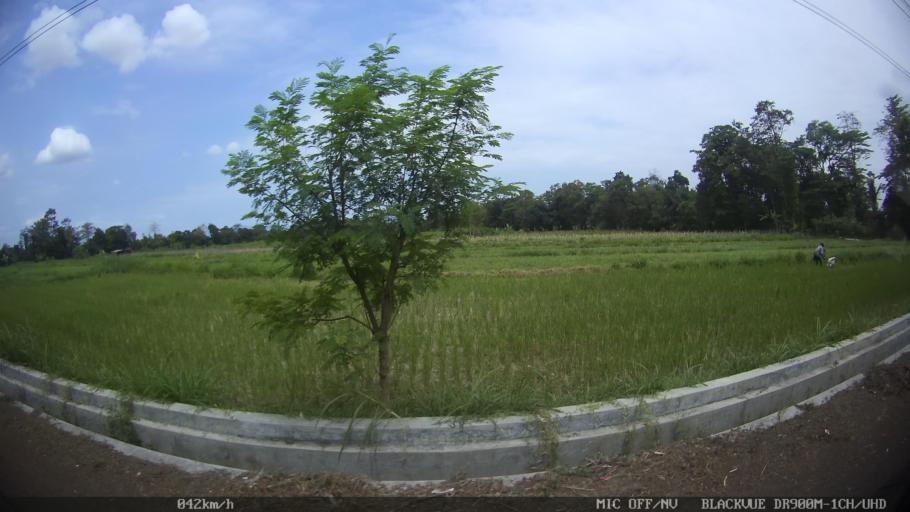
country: ID
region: Central Java
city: Candi Prambanan
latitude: -7.7295
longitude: 110.4643
